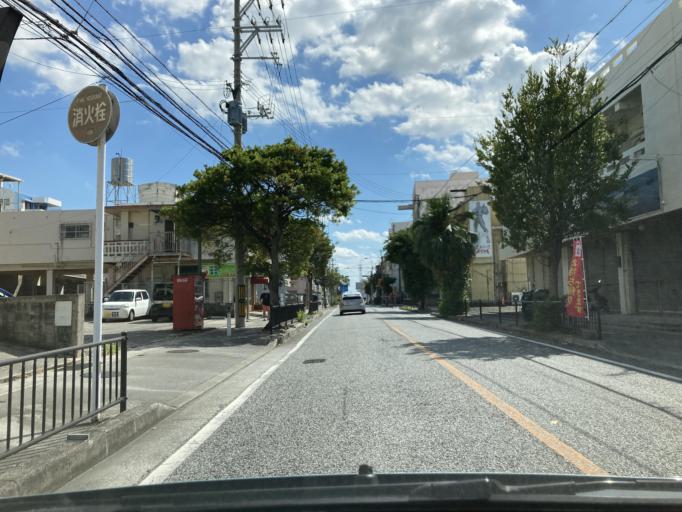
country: JP
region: Okinawa
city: Tomigusuku
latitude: 26.1946
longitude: 127.7057
